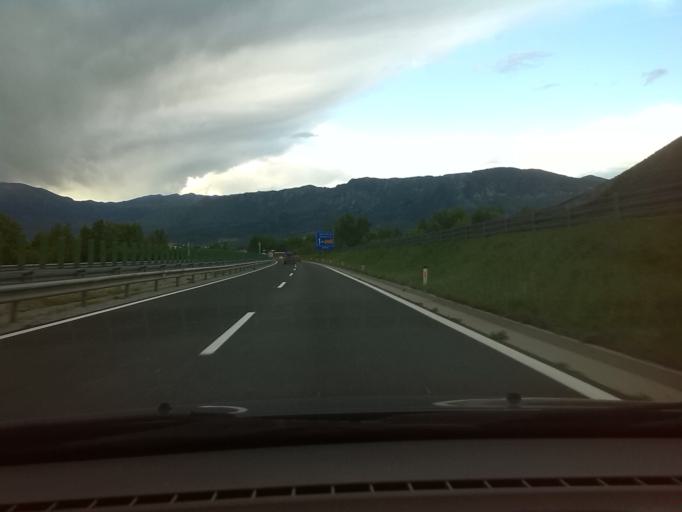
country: SI
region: Vipava
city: Vipava
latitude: 45.8230
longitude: 13.9609
